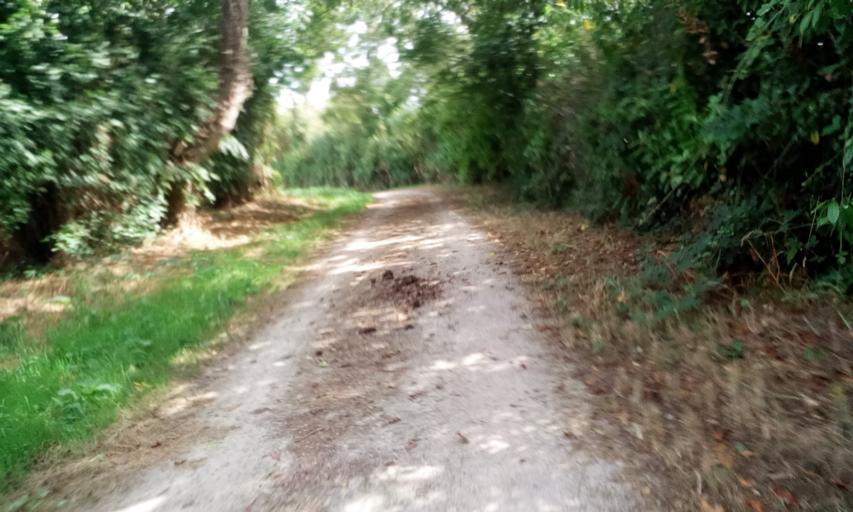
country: FR
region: Lower Normandy
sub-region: Departement du Calvados
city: Merville-Franceville-Plage
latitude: 49.2542
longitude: -0.1958
